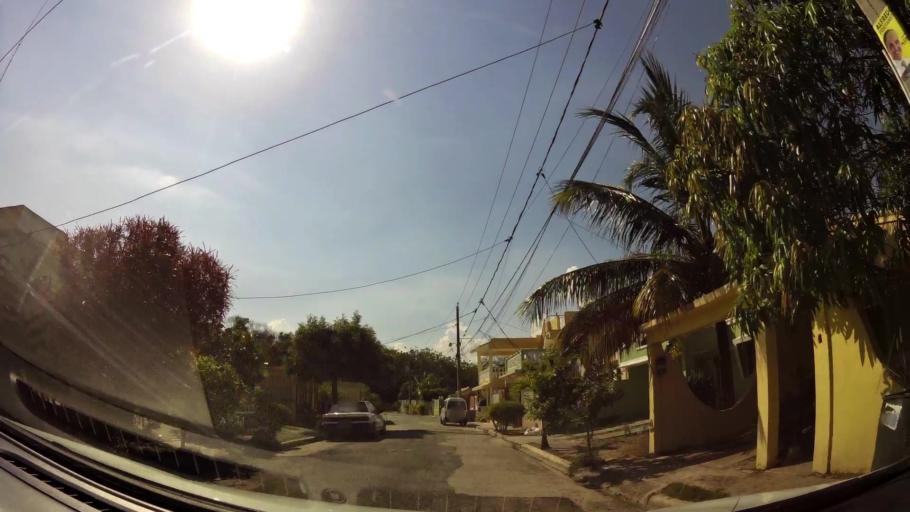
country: DO
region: Santo Domingo
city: Santo Domingo Oeste
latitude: 18.4733
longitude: -70.0111
